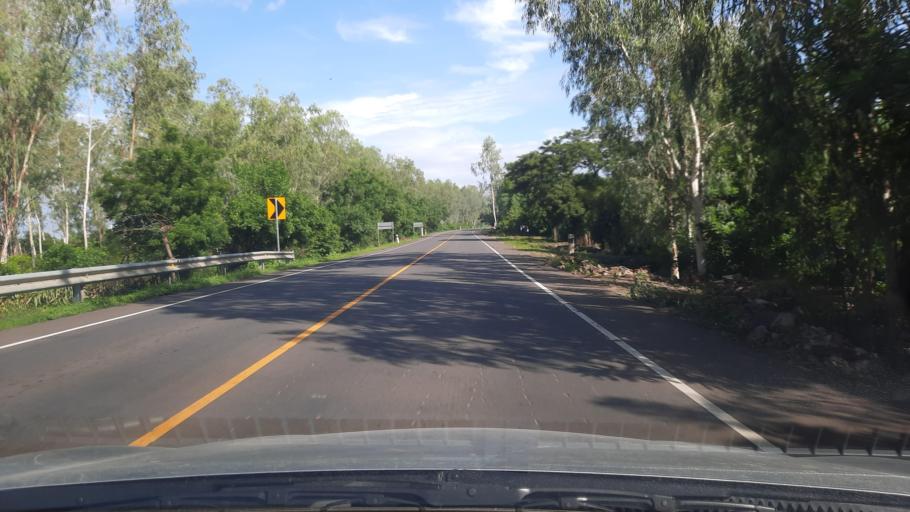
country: NI
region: Leon
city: Telica
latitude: 12.7337
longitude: -86.8814
